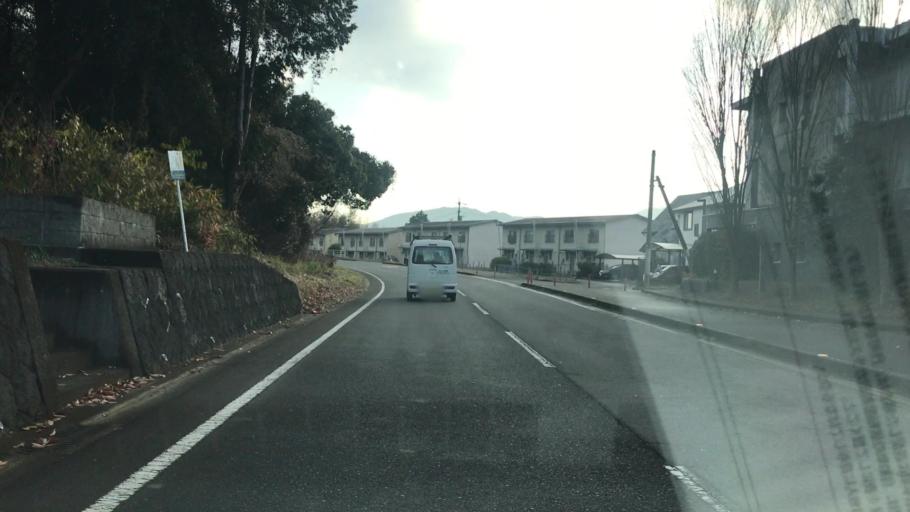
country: JP
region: Saga Prefecture
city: Takeocho-takeo
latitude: 33.2070
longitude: 130.0284
